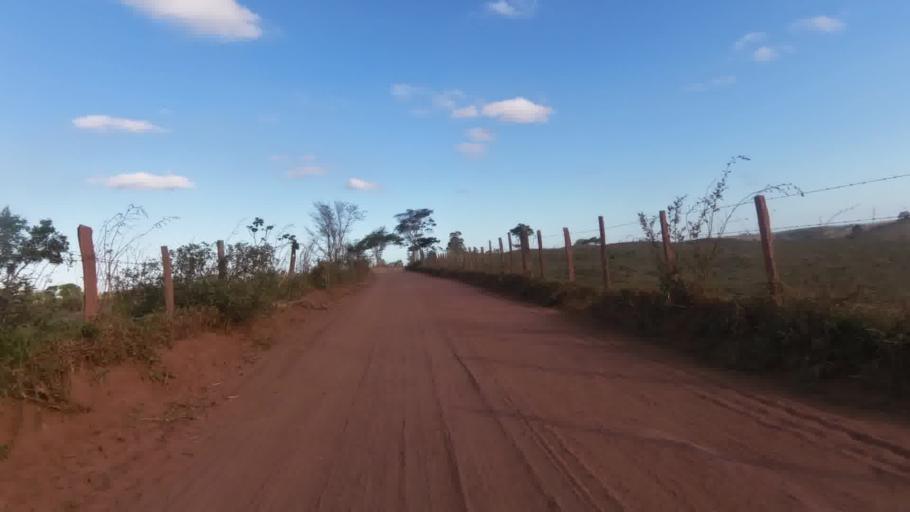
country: BR
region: Espirito Santo
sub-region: Marataizes
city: Marataizes
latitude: -21.1595
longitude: -41.0586
